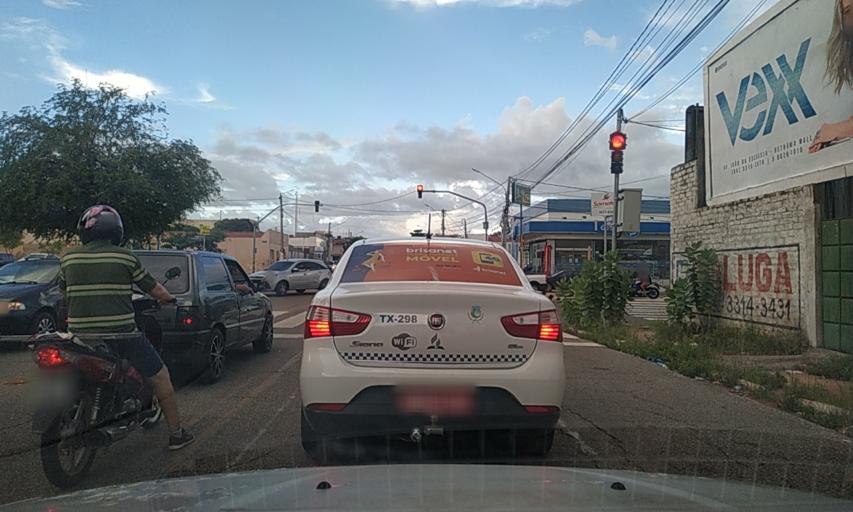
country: BR
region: Rio Grande do Norte
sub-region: Mossoro
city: Mossoro
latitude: -5.1896
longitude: -37.3467
